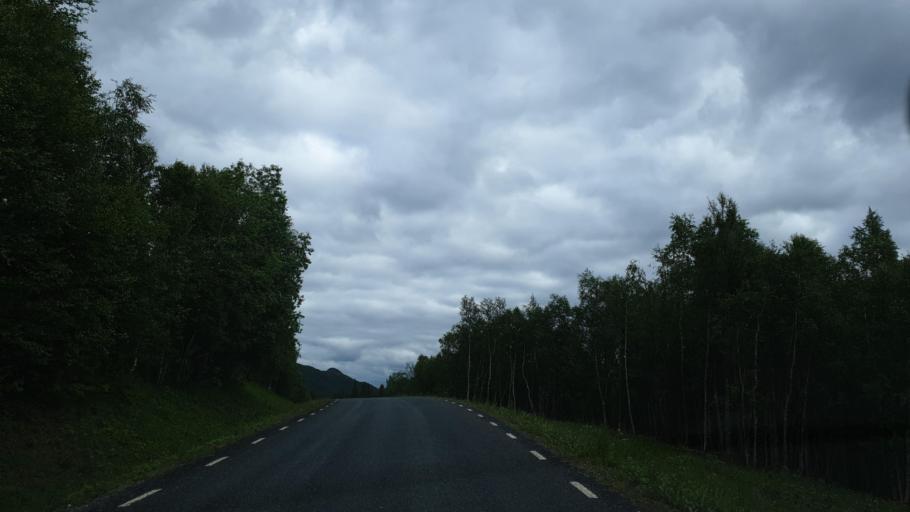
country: NO
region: Nordland
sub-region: Hattfjelldal
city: Hattfjelldal
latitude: 65.4449
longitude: 14.5331
